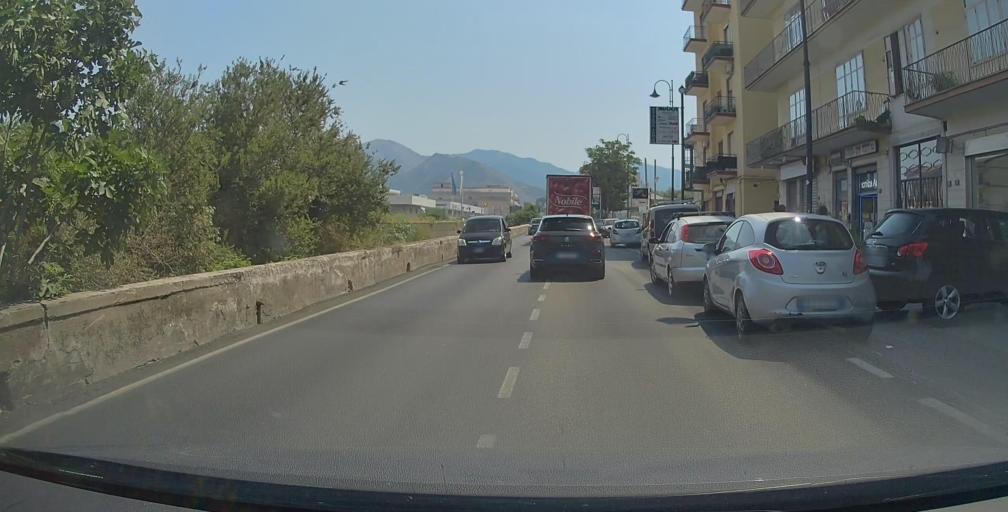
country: IT
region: Campania
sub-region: Provincia di Salerno
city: Nocera Inferiore
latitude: 40.7408
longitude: 14.6540
